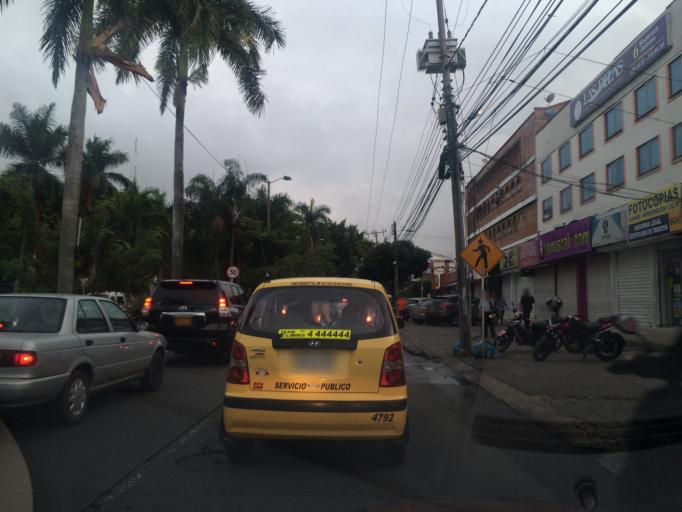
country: CO
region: Valle del Cauca
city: Cali
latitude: 3.4059
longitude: -76.5375
